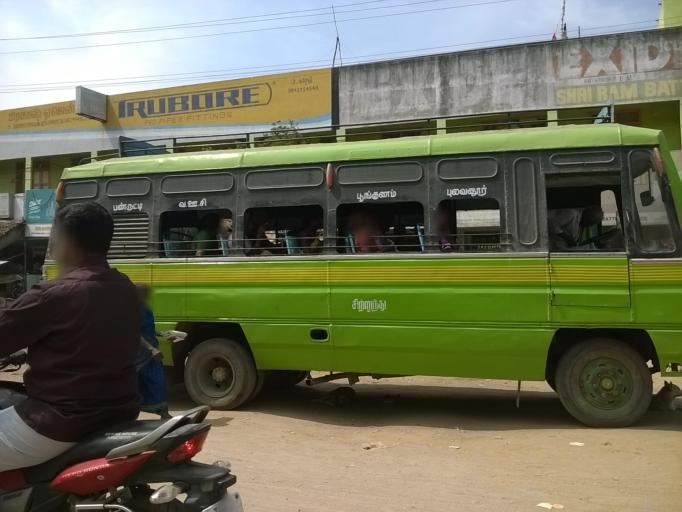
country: IN
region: Tamil Nadu
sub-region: Cuddalore
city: Panruti
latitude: 11.7781
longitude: 79.5537
